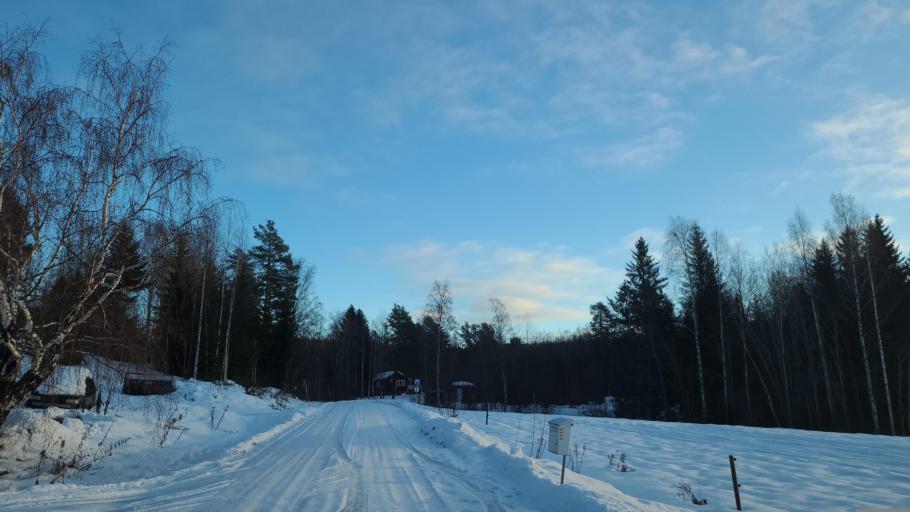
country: SE
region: Gaevleborg
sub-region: Bollnas Kommun
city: Kilafors
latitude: 61.3943
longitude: 16.6875
